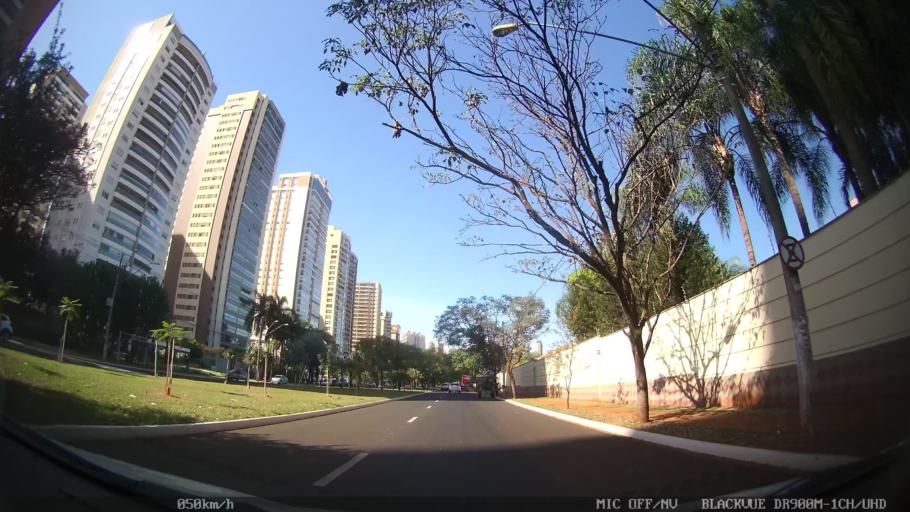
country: BR
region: Sao Paulo
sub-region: Ribeirao Preto
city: Ribeirao Preto
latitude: -21.2065
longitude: -47.8087
